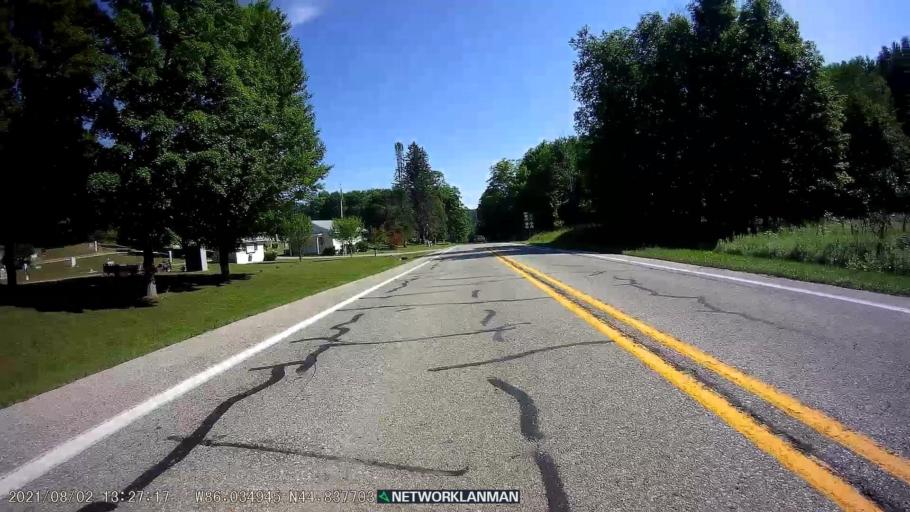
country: US
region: Michigan
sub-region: Benzie County
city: Beulah
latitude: 44.8377
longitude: -86.0349
